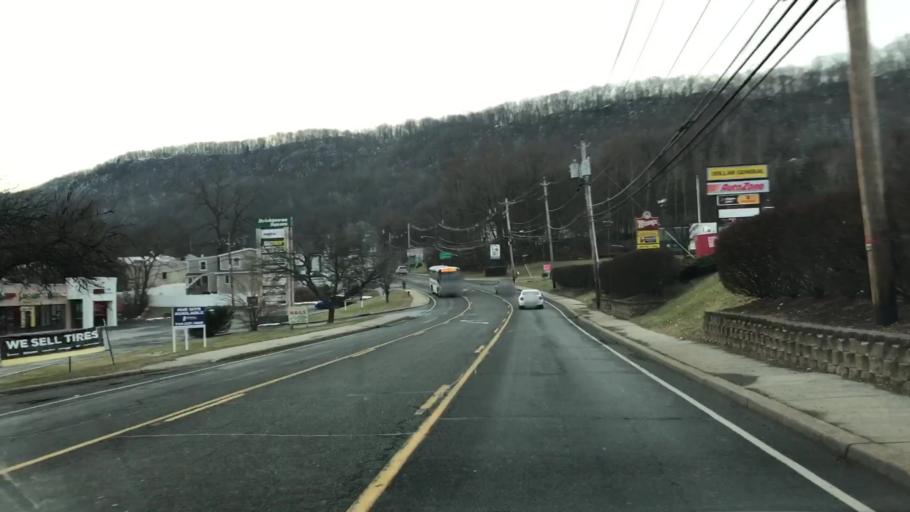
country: US
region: New York
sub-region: Rockland County
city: West Haverstraw
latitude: 41.2019
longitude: -73.9837
